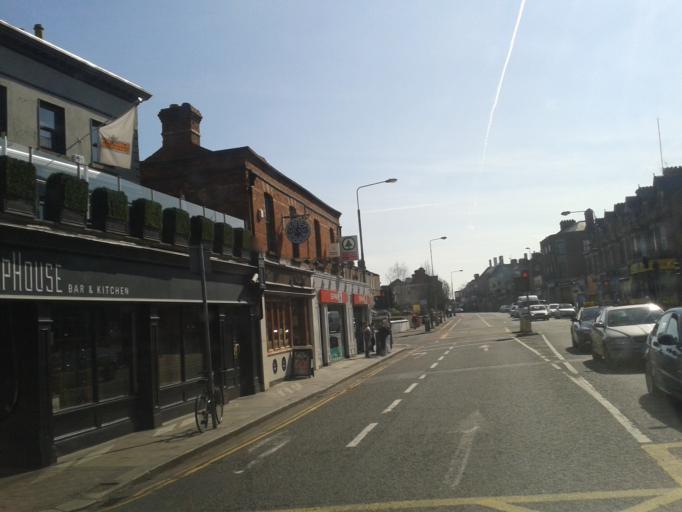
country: IE
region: Leinster
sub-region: Dublin City
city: Dublin
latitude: 53.3251
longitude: -6.2545
